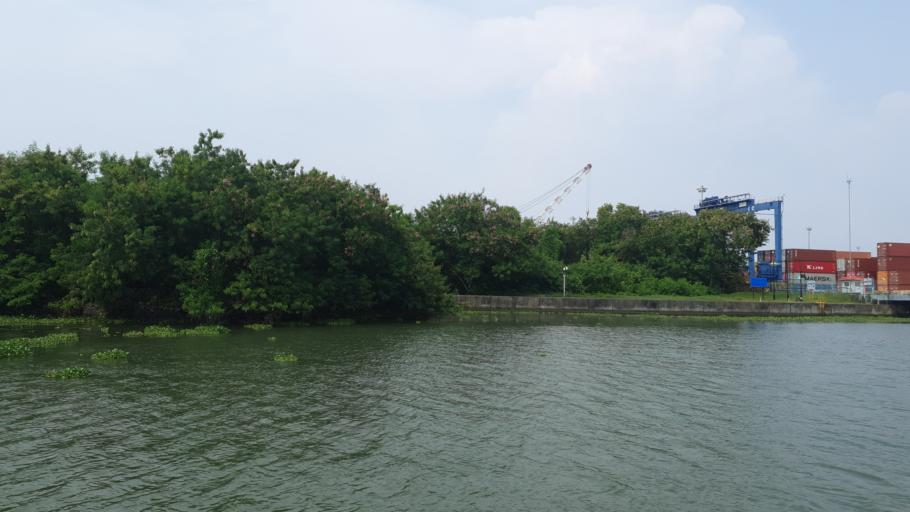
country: IN
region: Kerala
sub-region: Ernakulam
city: Cochin
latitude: 9.9760
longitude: 76.2492
